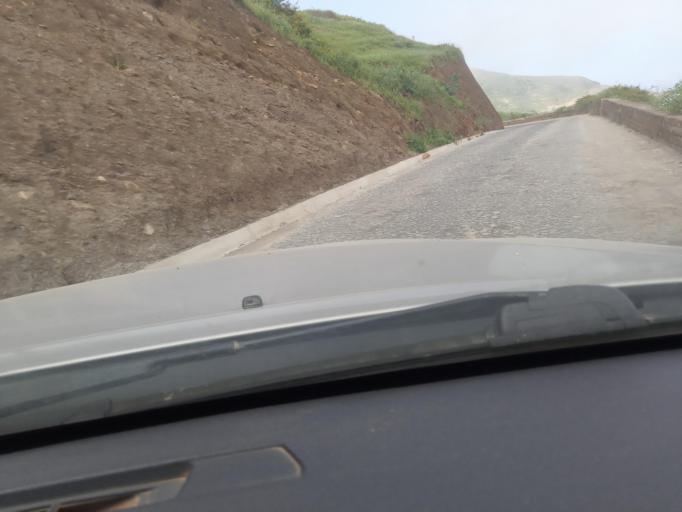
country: CV
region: Brava
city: Vila Nova Sintra
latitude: 14.8681
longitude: -24.7058
